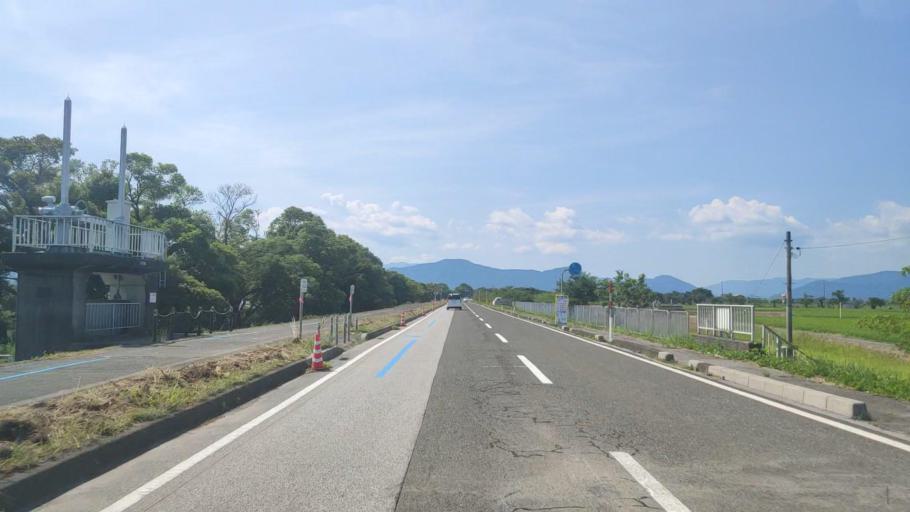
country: JP
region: Shiga Prefecture
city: Nagahama
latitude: 35.4371
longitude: 136.1938
